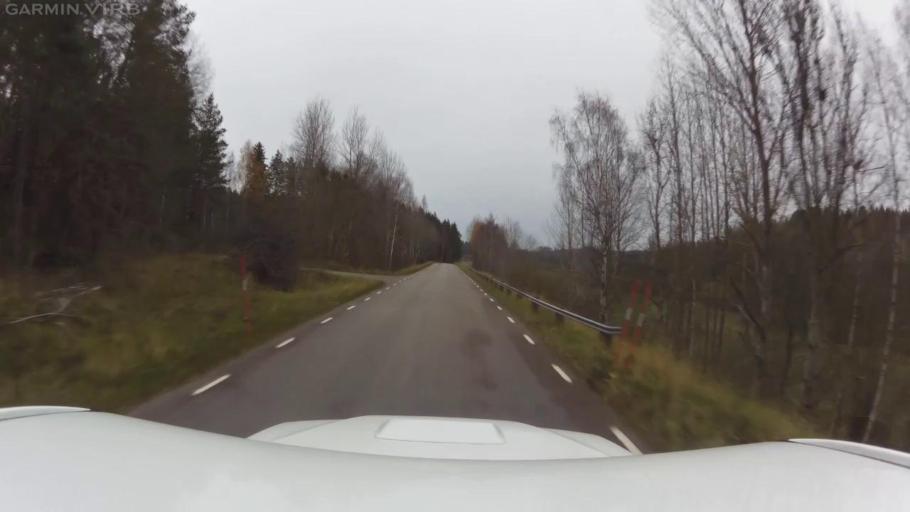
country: SE
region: OEstergoetland
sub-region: Linkopings Kommun
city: Vikingstad
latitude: 58.2235
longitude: 15.3963
